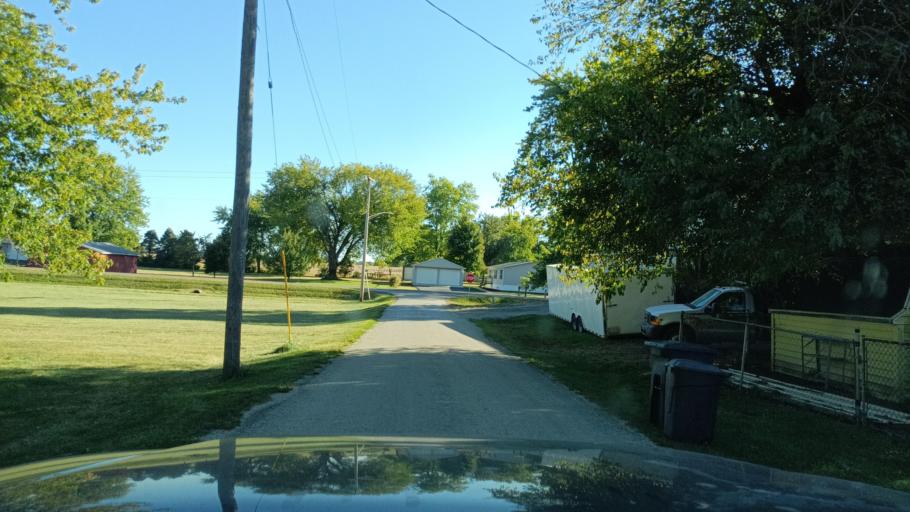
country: US
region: Illinois
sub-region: Logan County
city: Atlanta
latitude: 40.2390
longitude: -89.1222
